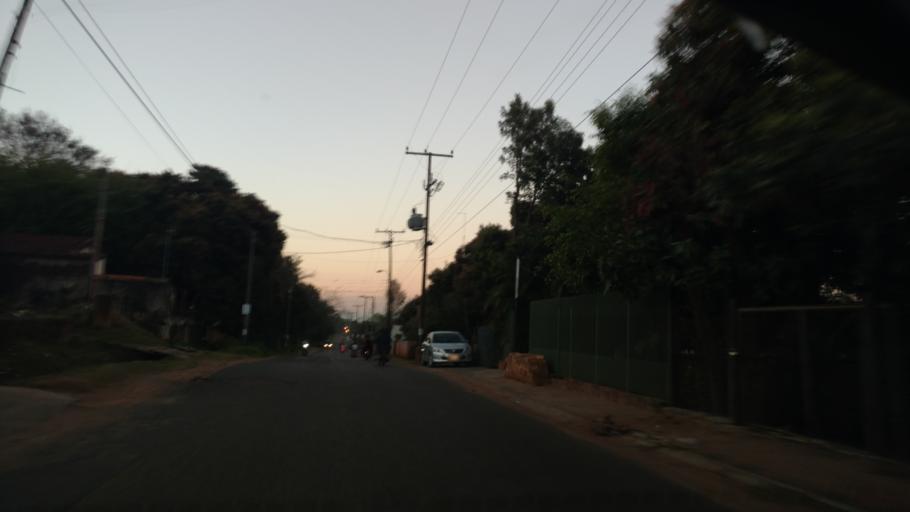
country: PY
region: Central
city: Guarambare
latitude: -25.4737
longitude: -57.4119
